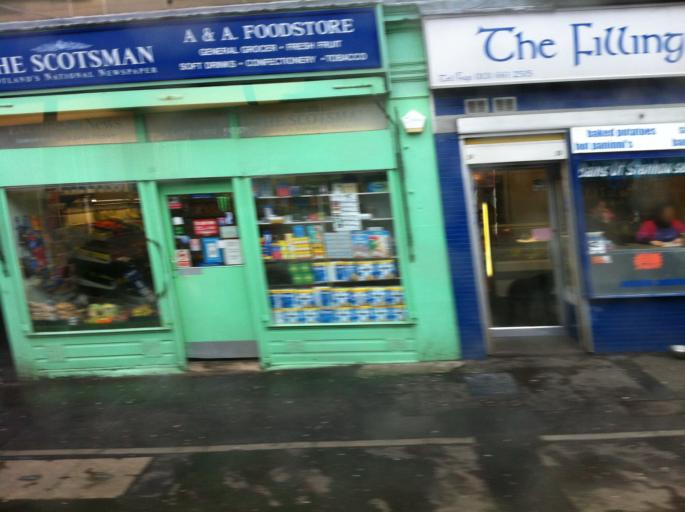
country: GB
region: Scotland
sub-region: West Lothian
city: Seafield
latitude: 55.9585
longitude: -3.1718
